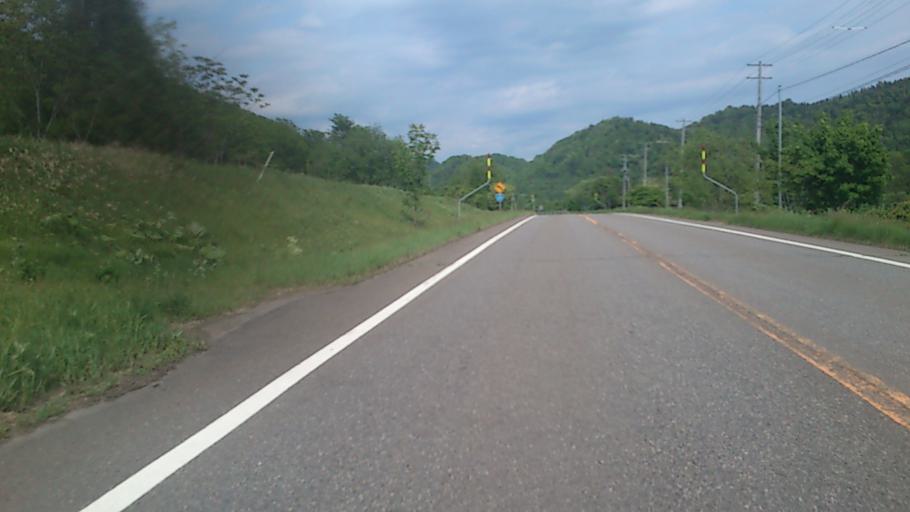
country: JP
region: Hokkaido
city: Kitami
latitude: 43.3433
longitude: 143.7655
